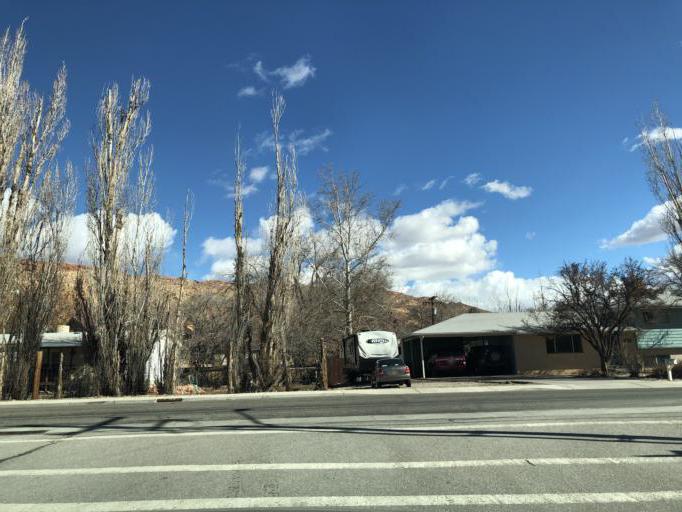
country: US
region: Utah
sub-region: Grand County
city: Moab
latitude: 38.5848
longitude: -109.5613
